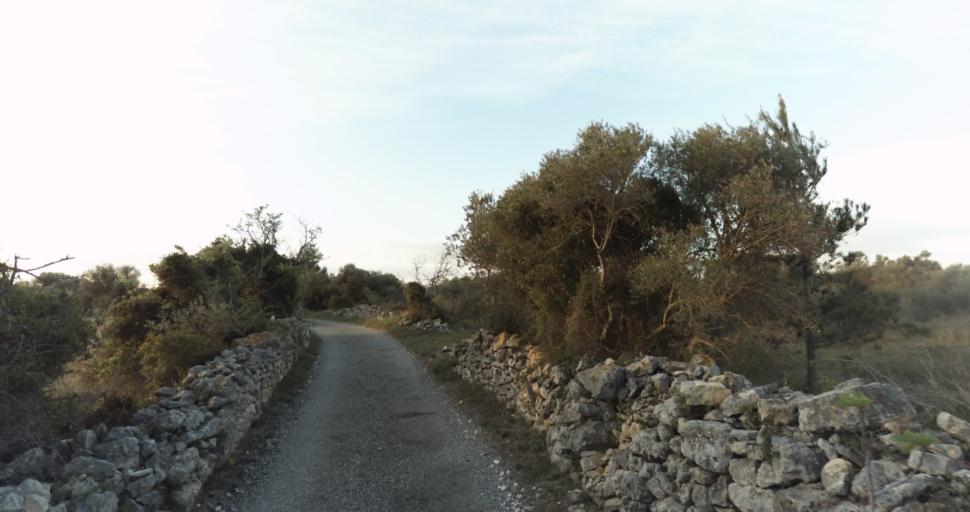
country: FR
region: Languedoc-Roussillon
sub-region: Departement de l'Aude
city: Leucate
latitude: 42.9294
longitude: 3.0191
